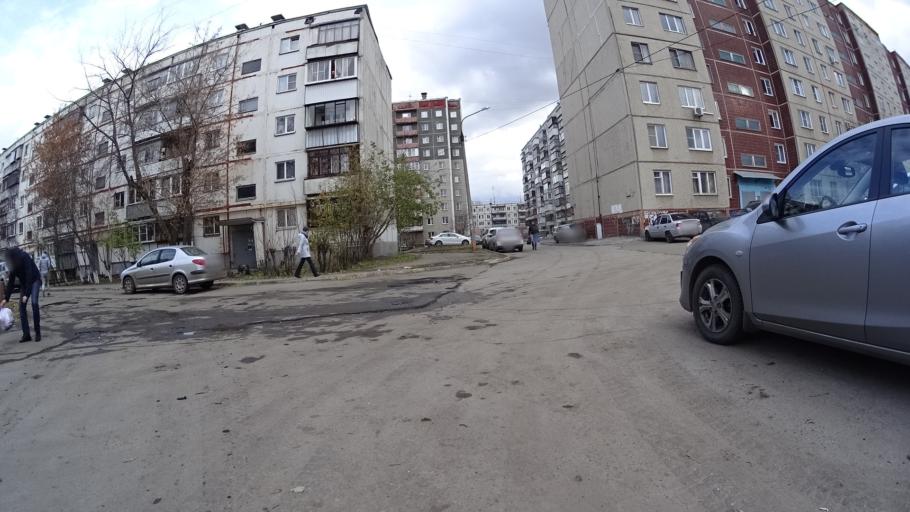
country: RU
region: Chelyabinsk
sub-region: Gorod Chelyabinsk
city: Chelyabinsk
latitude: 55.1929
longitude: 61.3130
